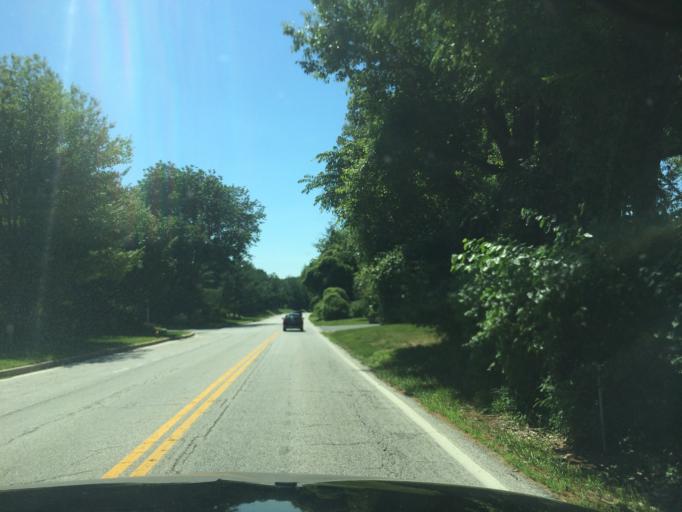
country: US
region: Maryland
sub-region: Baltimore County
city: Mays Chapel
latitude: 39.4261
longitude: -76.6621
